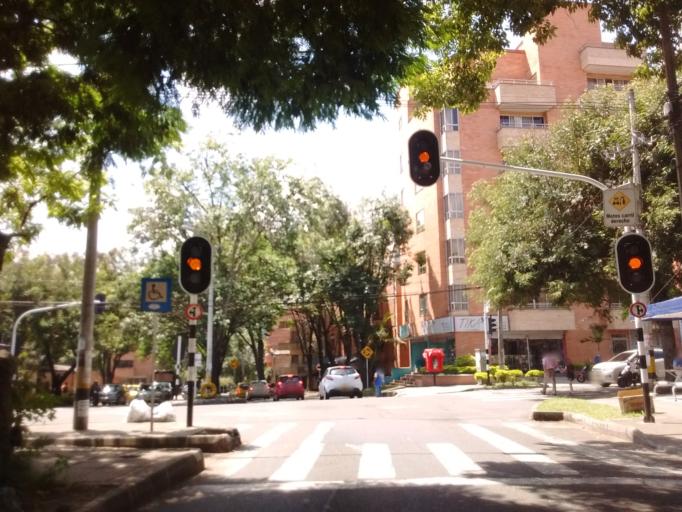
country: CO
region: Antioquia
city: Medellin
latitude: 6.2426
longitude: -75.6004
